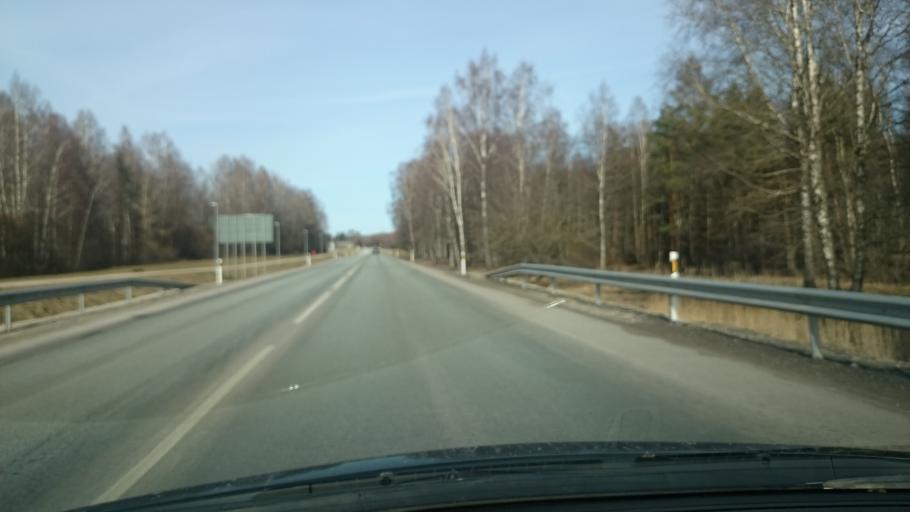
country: EE
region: Jaervamaa
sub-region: Paide linn
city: Paide
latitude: 58.8969
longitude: 25.5722
